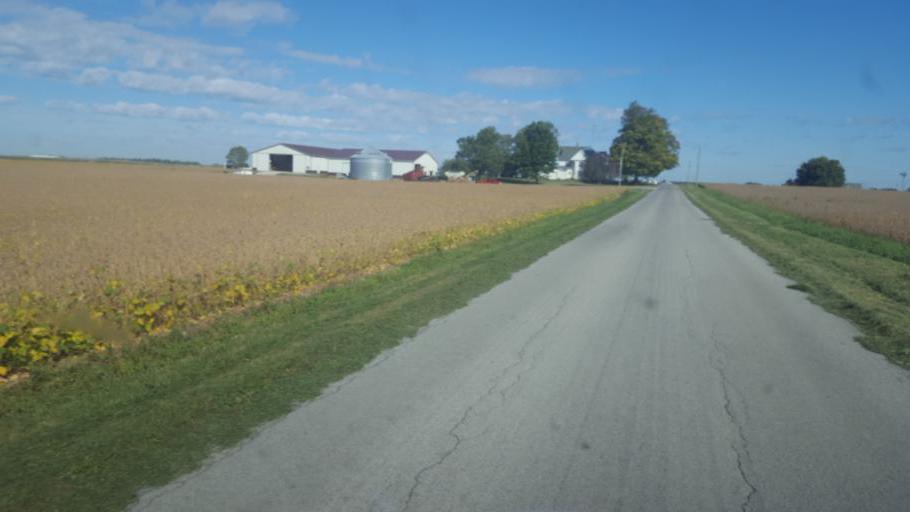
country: US
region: Ohio
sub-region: Wyandot County
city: Upper Sandusky
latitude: 40.7991
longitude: -83.2173
